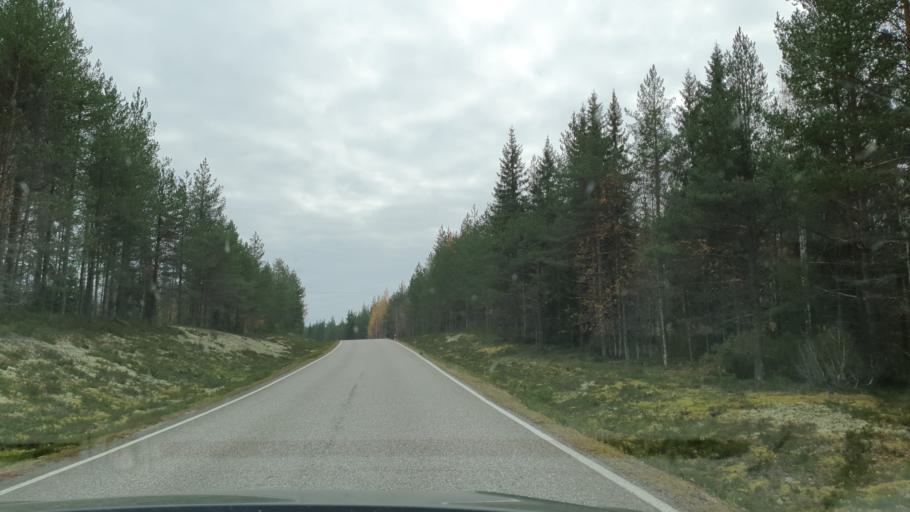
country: FI
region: Kainuu
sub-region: Kajaani
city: Ristijaervi
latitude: 64.6176
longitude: 27.9941
